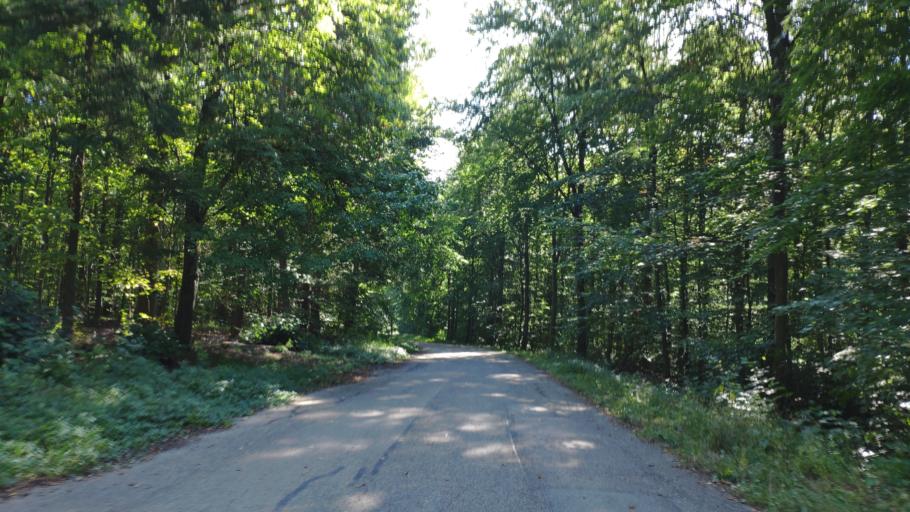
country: DE
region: Baden-Wuerttemberg
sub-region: Tuebingen Region
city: Ulm
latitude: 48.4184
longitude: 9.9554
